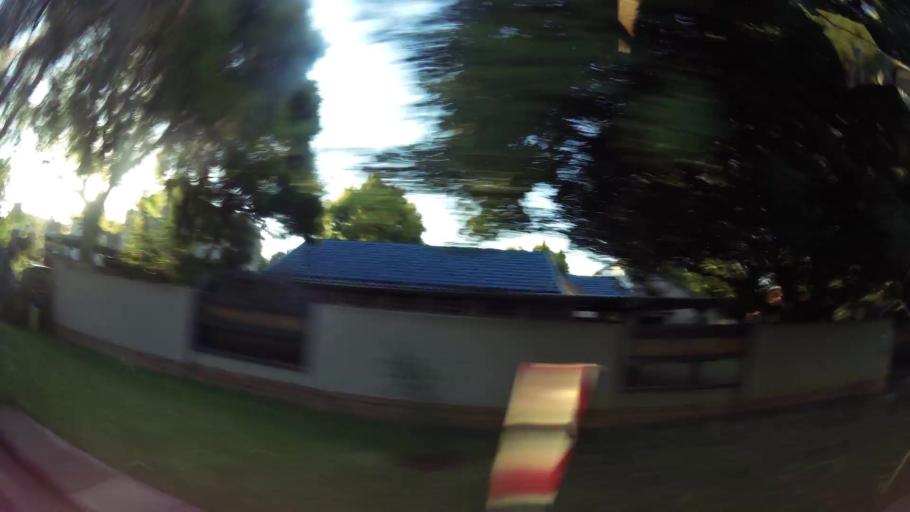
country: ZA
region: Gauteng
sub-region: City of Tshwane Metropolitan Municipality
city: Centurion
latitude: -25.8727
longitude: 28.1472
